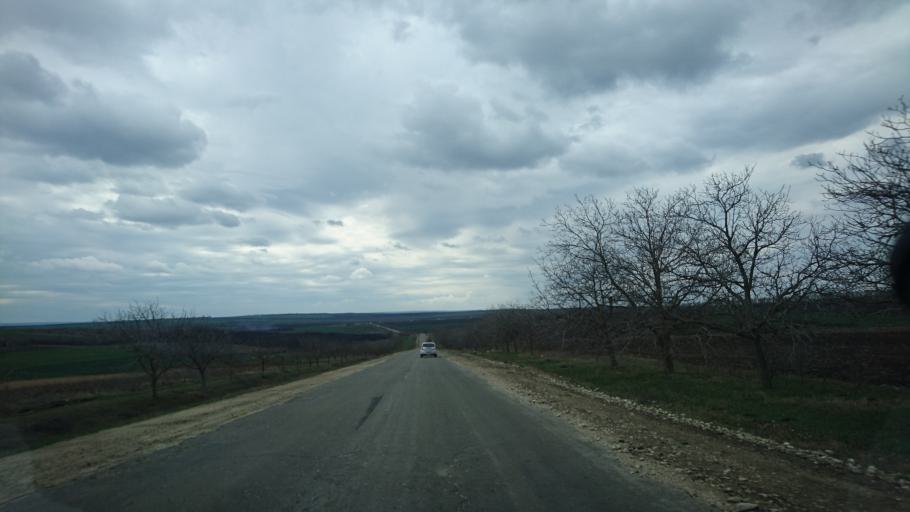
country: MD
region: Gagauzia
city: Comrat
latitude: 46.3092
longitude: 28.6012
